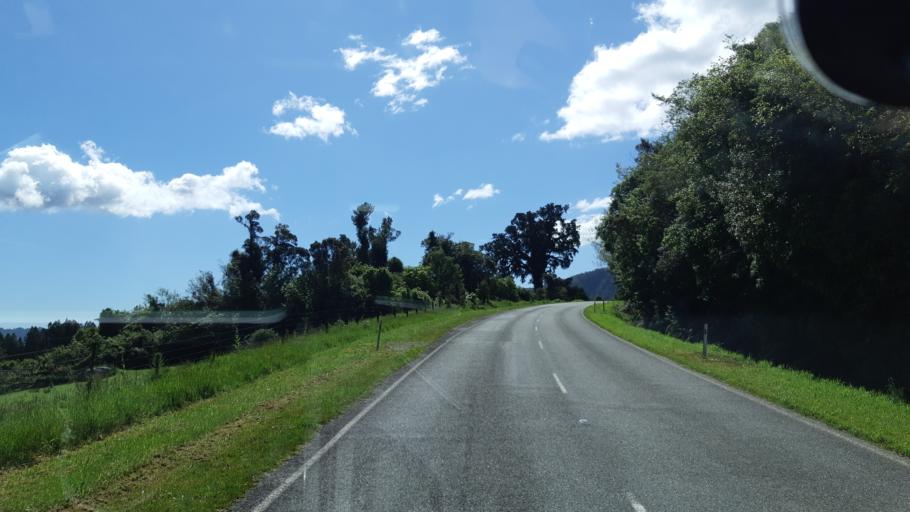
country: NZ
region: West Coast
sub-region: Westland District
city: Hokitika
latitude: -43.0907
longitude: 170.6277
